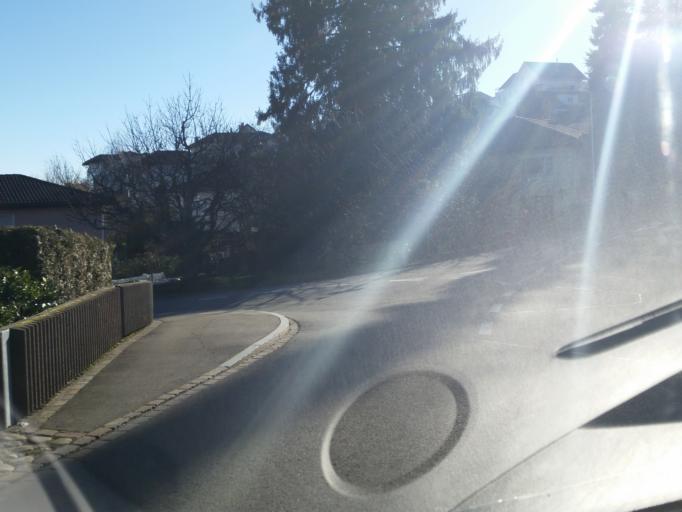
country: CH
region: Zurich
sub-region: Bezirk Dietikon
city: Dietikon / Almend
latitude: 47.3976
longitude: 8.3767
